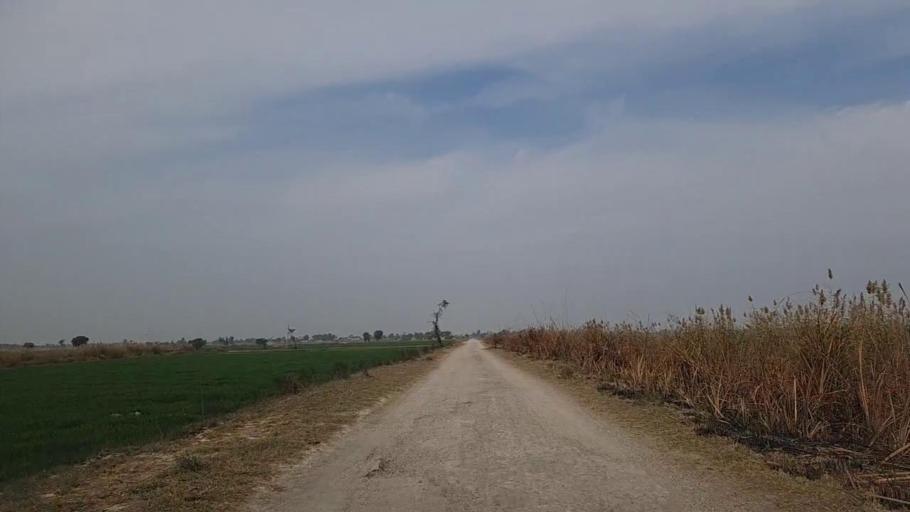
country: PK
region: Sindh
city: Daur
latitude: 26.4718
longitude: 68.4024
